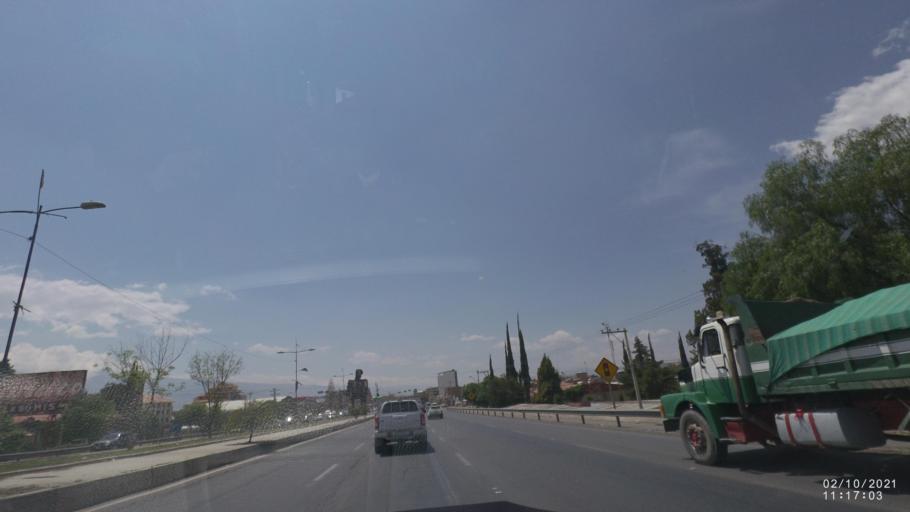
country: BO
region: Cochabamba
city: Sipe Sipe
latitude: -17.3949
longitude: -66.2930
